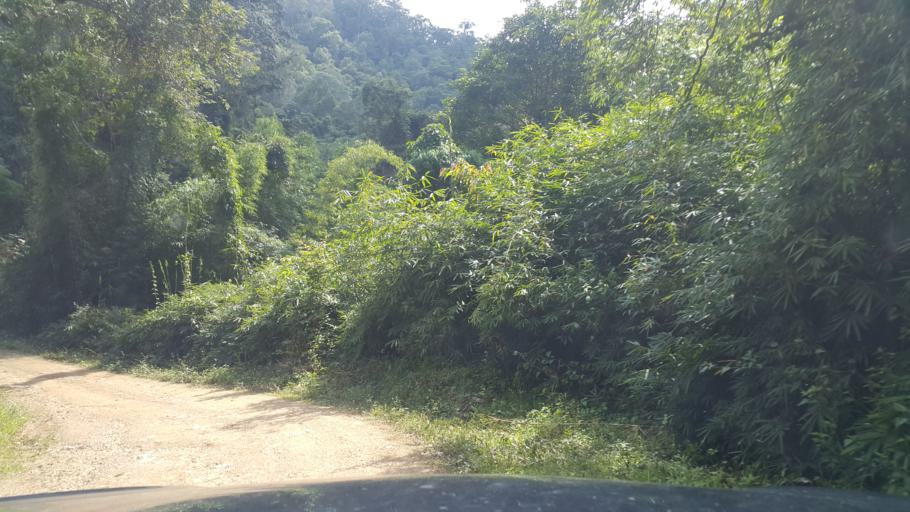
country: TH
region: Chiang Mai
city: Phrao
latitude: 19.0932
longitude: 99.2631
